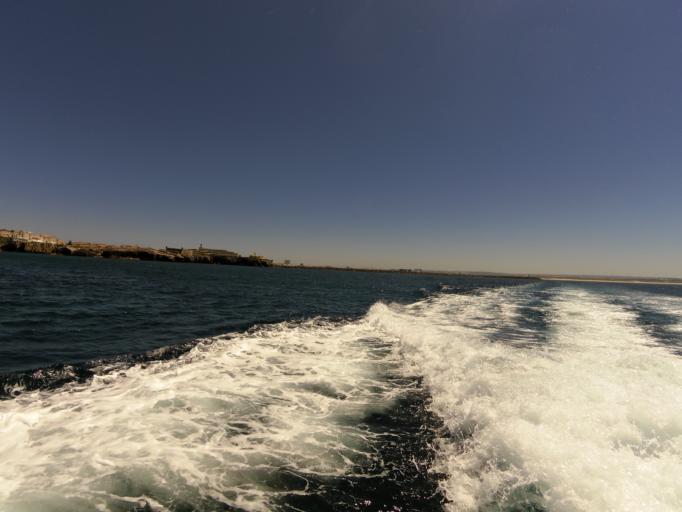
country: PT
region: Leiria
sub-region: Peniche
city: Peniche
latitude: 39.3496
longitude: -9.3868
